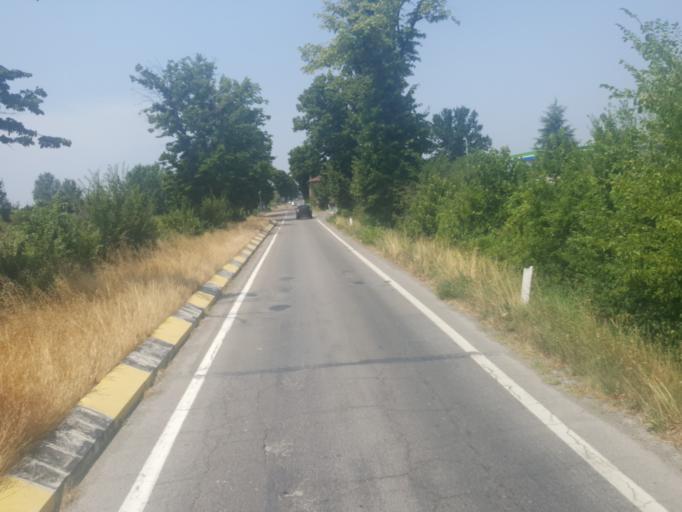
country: IT
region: Emilia-Romagna
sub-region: Provincia di Modena
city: Manzolino
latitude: 44.5849
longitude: 11.0816
